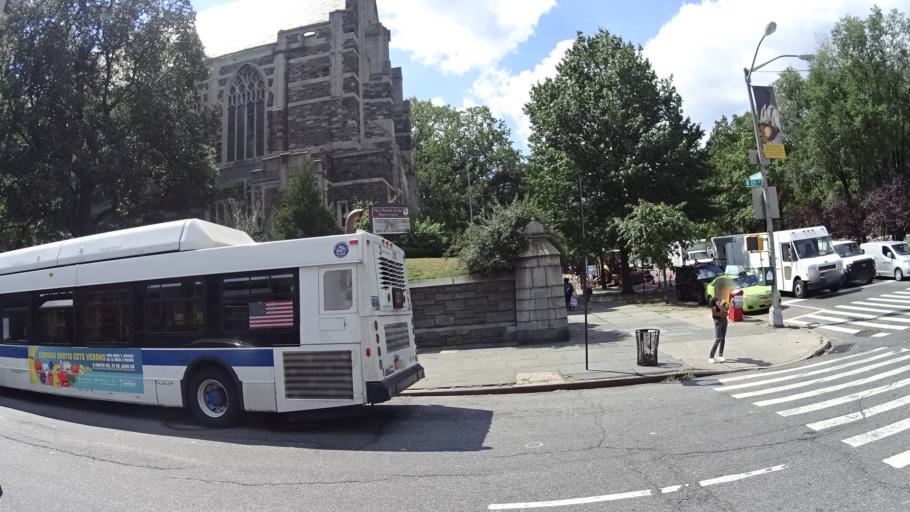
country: US
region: New Jersey
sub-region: Bergen County
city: Fort Lee
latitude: 40.8327
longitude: -73.9455
